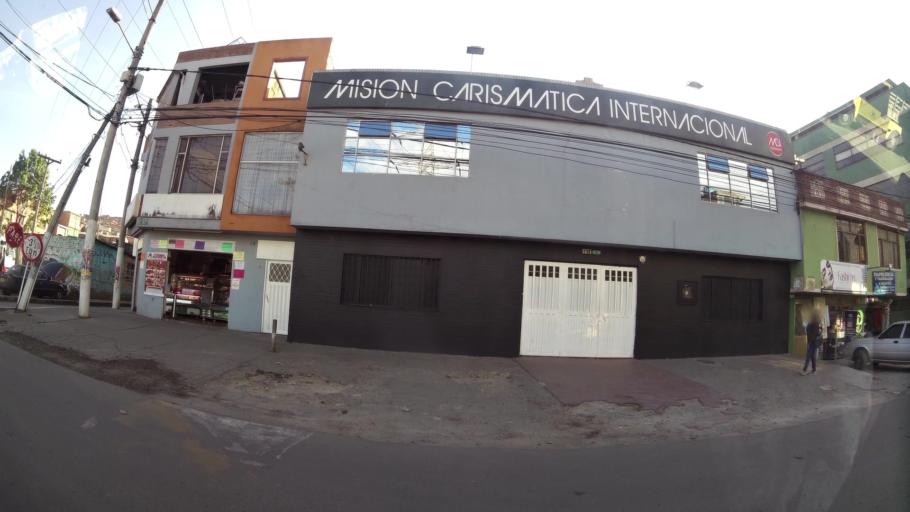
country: CO
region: Cundinamarca
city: Soacha
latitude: 4.5755
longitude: -74.1532
